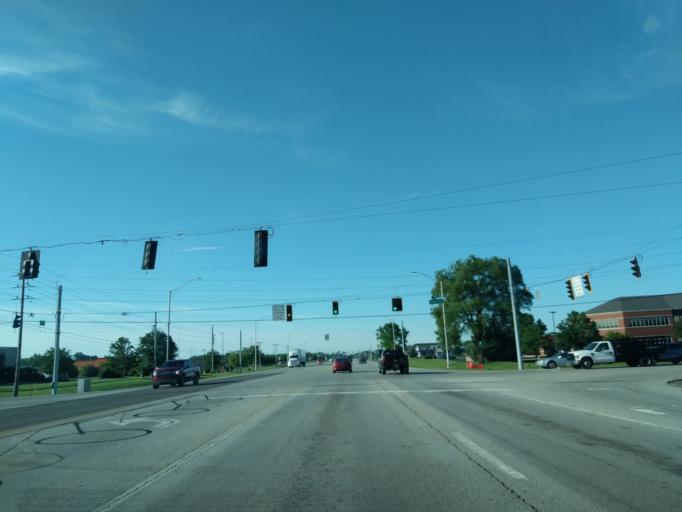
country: US
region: Indiana
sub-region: Hancock County
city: Greenfield
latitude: 39.8145
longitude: -85.7699
